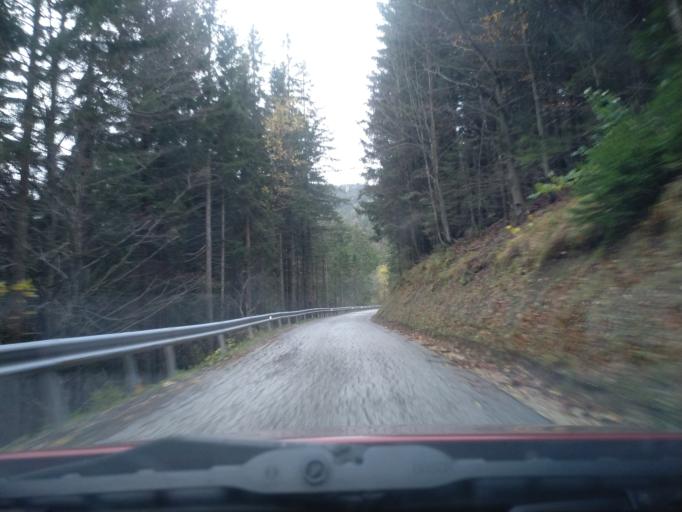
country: SI
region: Kamnik
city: Mekinje
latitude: 46.2781
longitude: 14.6912
